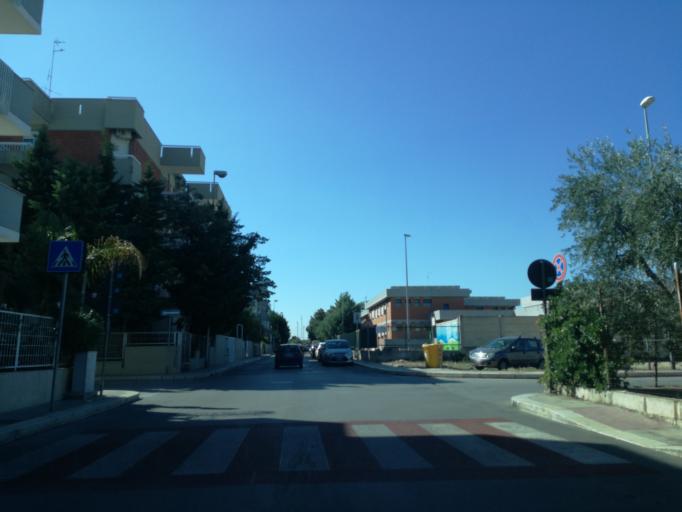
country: IT
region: Apulia
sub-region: Provincia di Bari
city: Capurso
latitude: 41.0490
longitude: 16.9153
